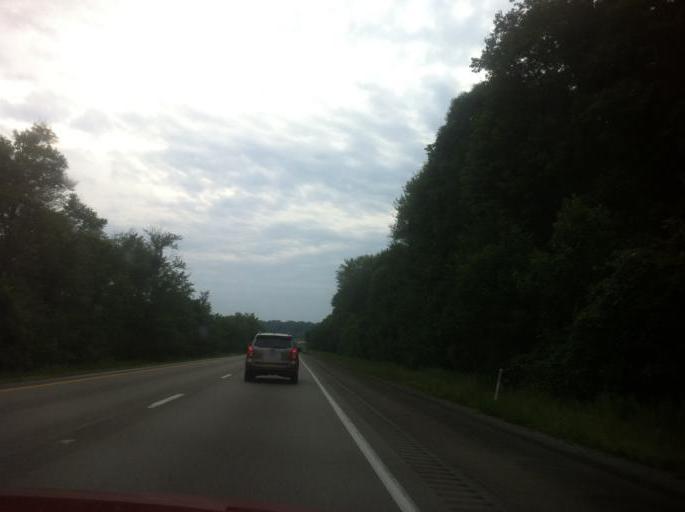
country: US
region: Pennsylvania
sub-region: Mercer County
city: Grove City
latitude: 41.2022
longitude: -80.0066
